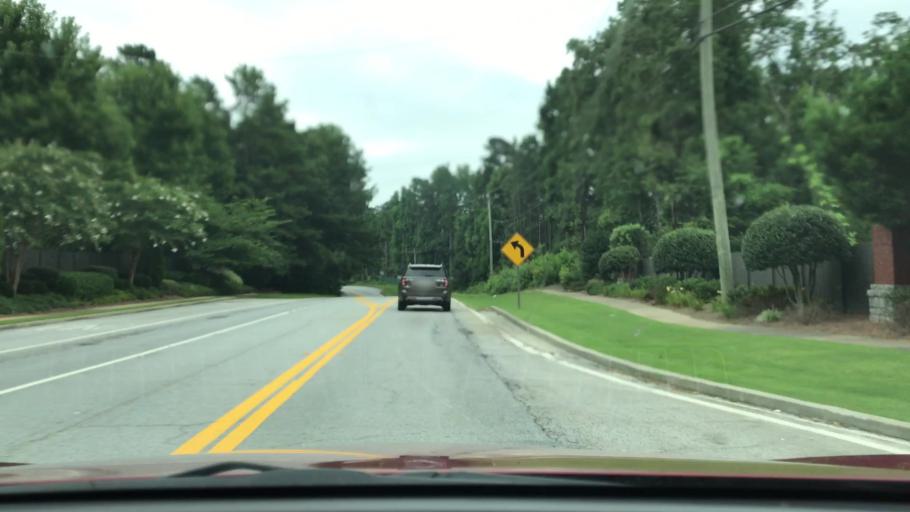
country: US
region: Georgia
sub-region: Gwinnett County
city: Suwanee
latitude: 34.0029
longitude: -84.0622
